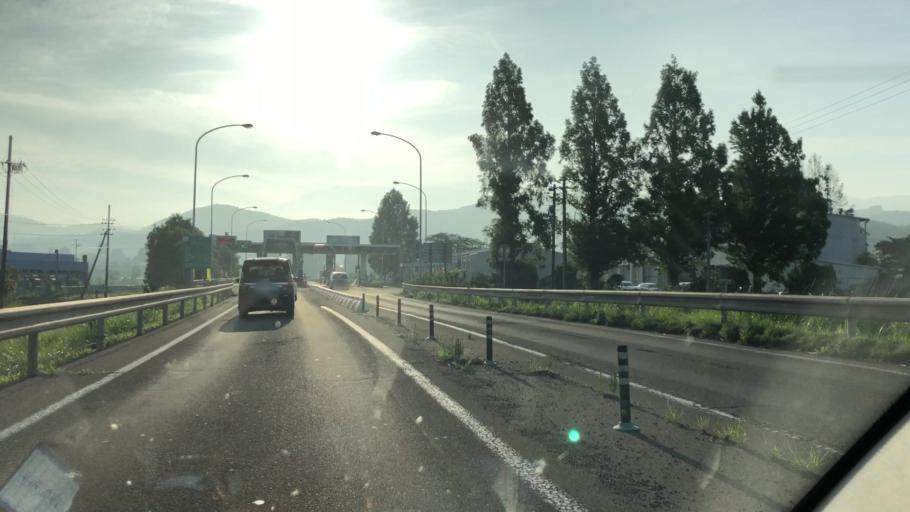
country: JP
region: Miyagi
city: Shiroishi
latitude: 38.0375
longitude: 140.6384
